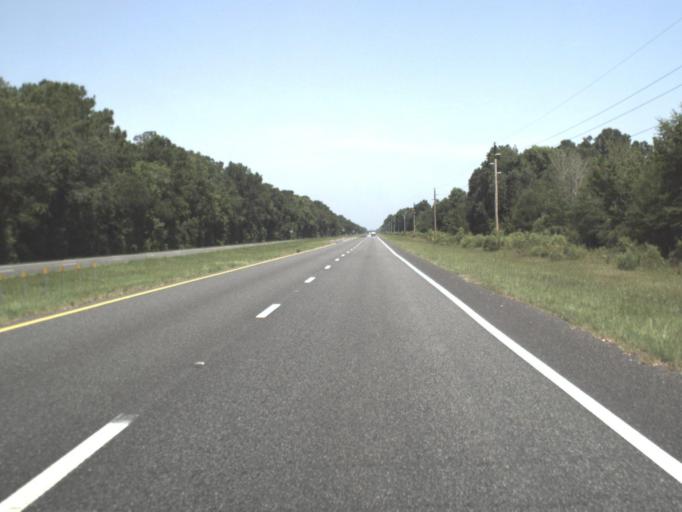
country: US
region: Florida
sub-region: Taylor County
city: Steinhatchee
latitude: 29.6834
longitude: -83.2637
